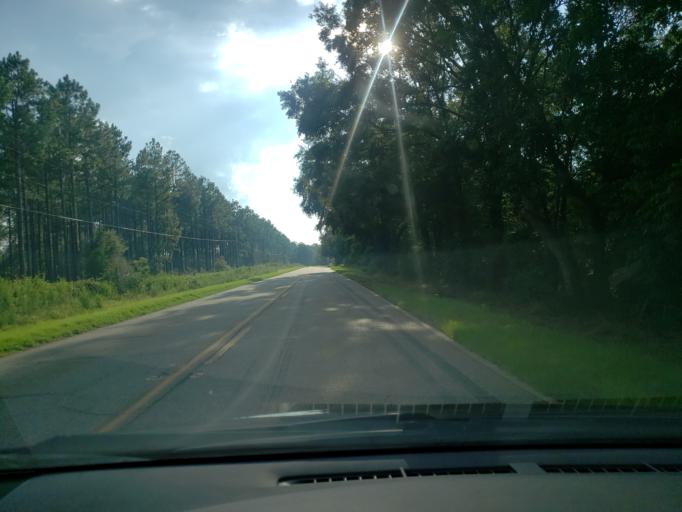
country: US
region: Georgia
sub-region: Dougherty County
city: Albany
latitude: 31.5731
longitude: -84.3259
